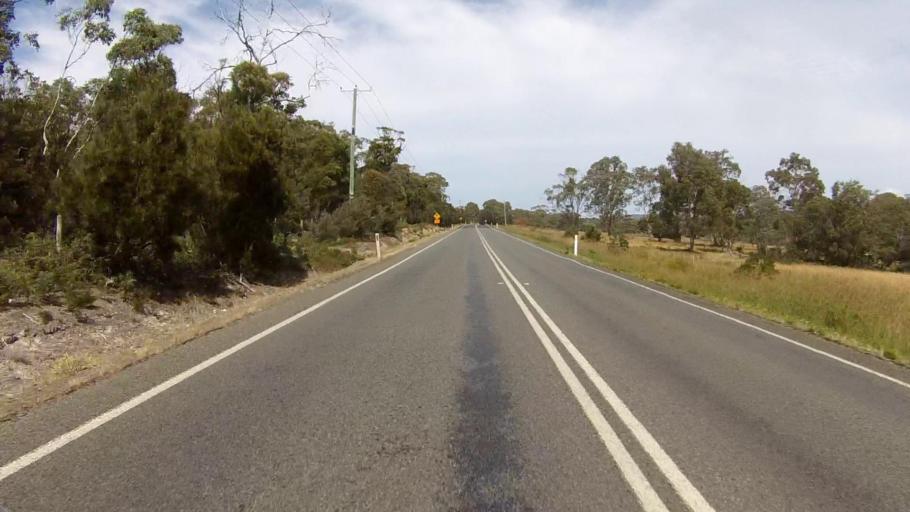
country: AU
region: Tasmania
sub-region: Clarence
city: Sandford
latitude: -42.9944
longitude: 147.4999
